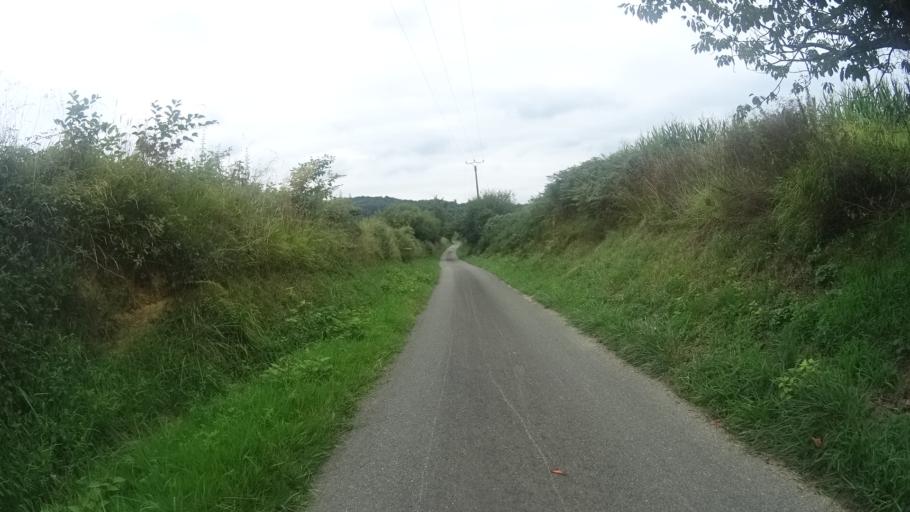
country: FR
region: Aquitaine
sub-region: Departement des Pyrenees-Atlantiques
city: Mont
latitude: 43.4800
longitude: -0.6943
